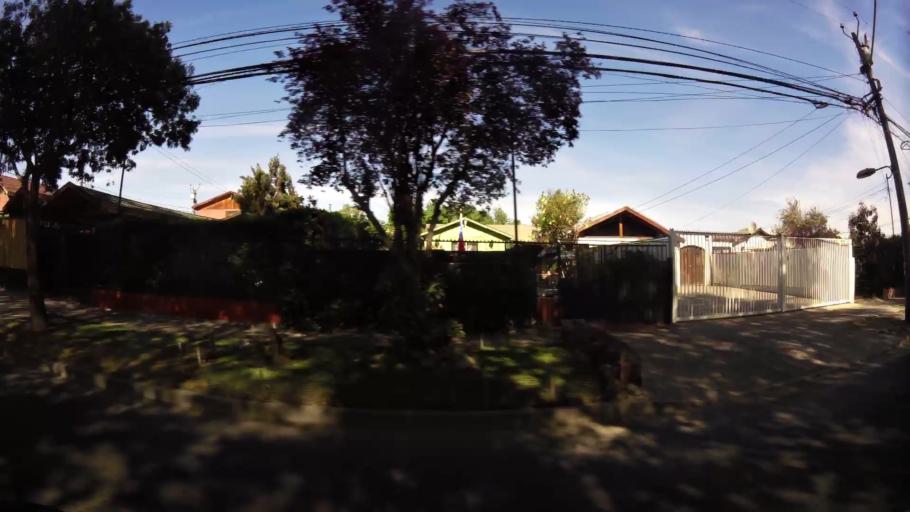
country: CL
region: Santiago Metropolitan
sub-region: Provincia de Santiago
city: Lo Prado
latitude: -33.4810
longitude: -70.7442
